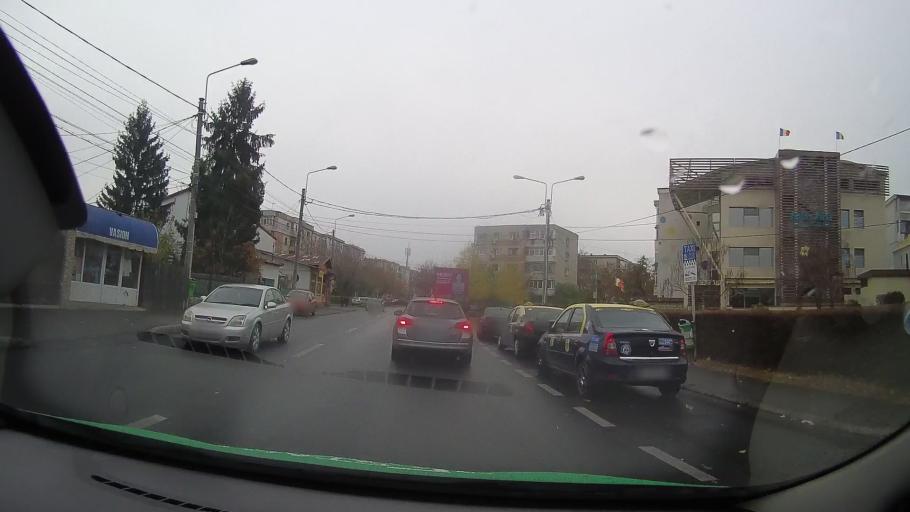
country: RO
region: Prahova
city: Ploiesti
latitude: 44.9317
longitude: 26.0047
